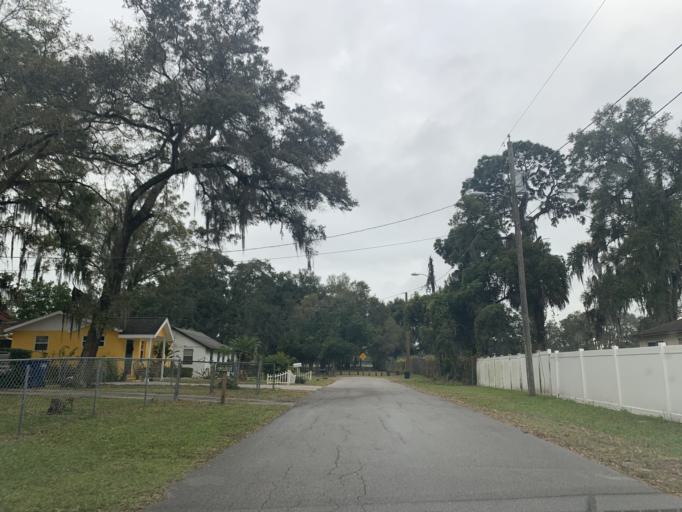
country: US
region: Florida
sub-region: Hillsborough County
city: East Lake-Orient Park
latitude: 27.9939
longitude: -82.4080
